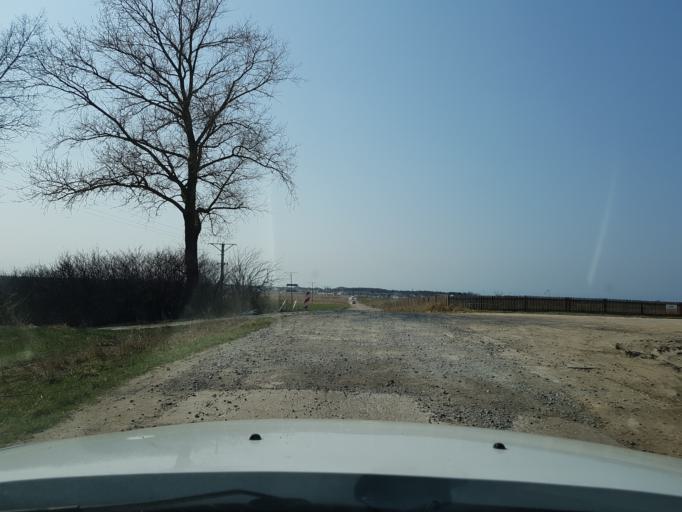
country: PL
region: West Pomeranian Voivodeship
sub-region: Powiat slawienski
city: Darlowo
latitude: 54.4435
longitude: 16.4165
